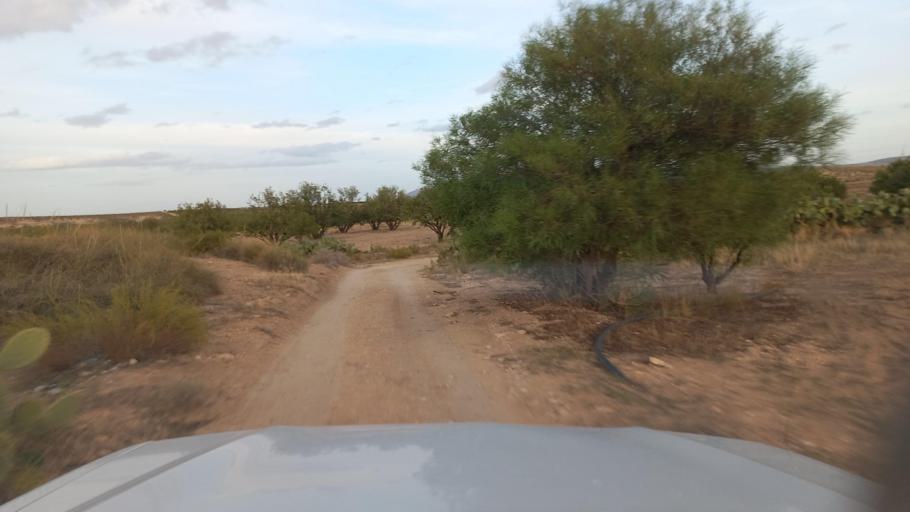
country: TN
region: Al Qasrayn
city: Sbiba
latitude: 35.4098
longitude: 9.0856
